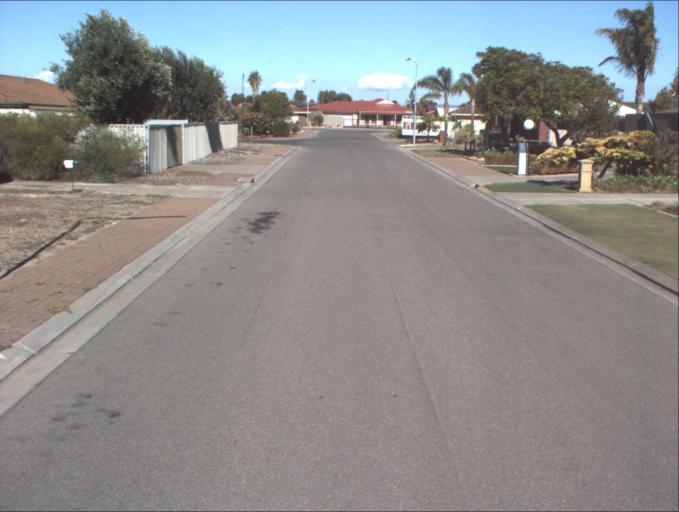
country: AU
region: South Australia
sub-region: Port Adelaide Enfield
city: Birkenhead
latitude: -34.7818
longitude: 138.4910
